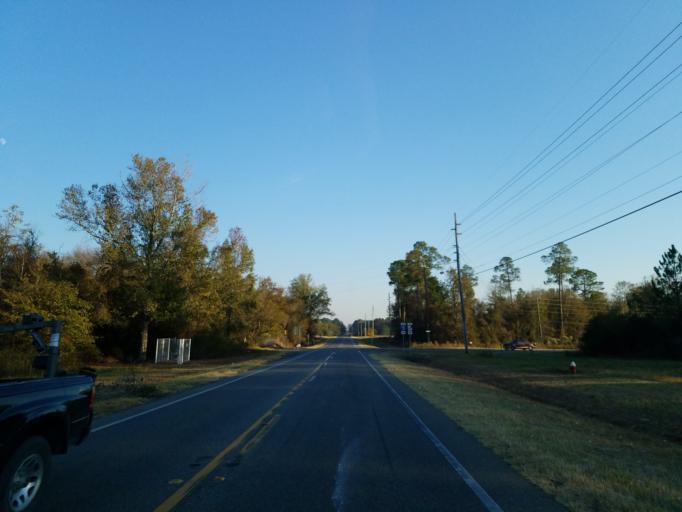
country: US
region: Georgia
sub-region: Crisp County
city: Cordele
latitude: 31.9432
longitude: -83.7392
